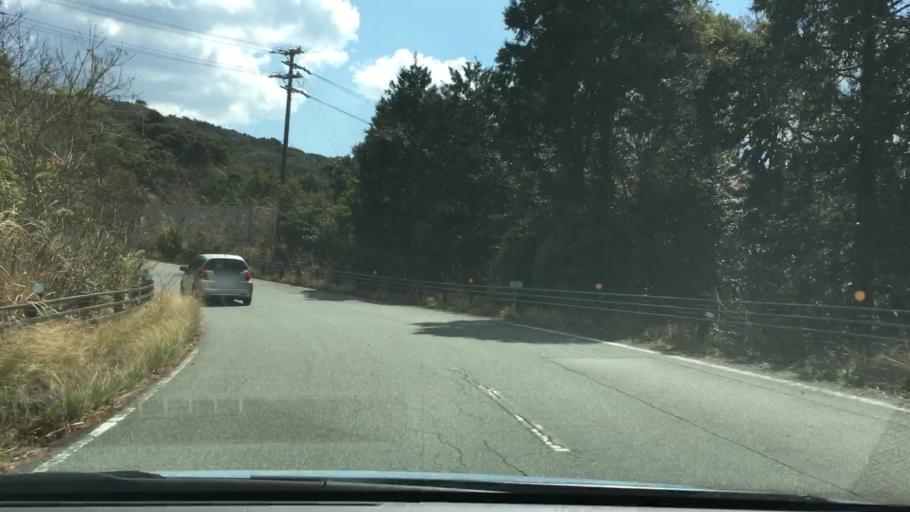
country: JP
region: Mie
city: Toba
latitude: 34.4410
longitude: 136.8931
